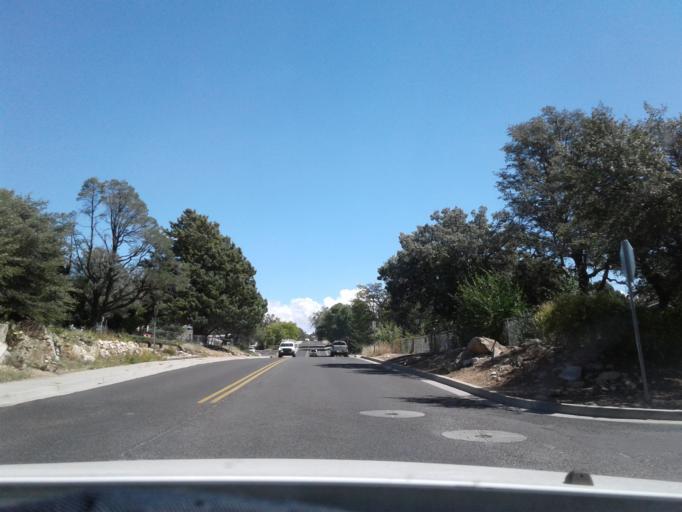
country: US
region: Arizona
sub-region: Yavapai County
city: Prescott
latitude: 34.5708
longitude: -112.4794
